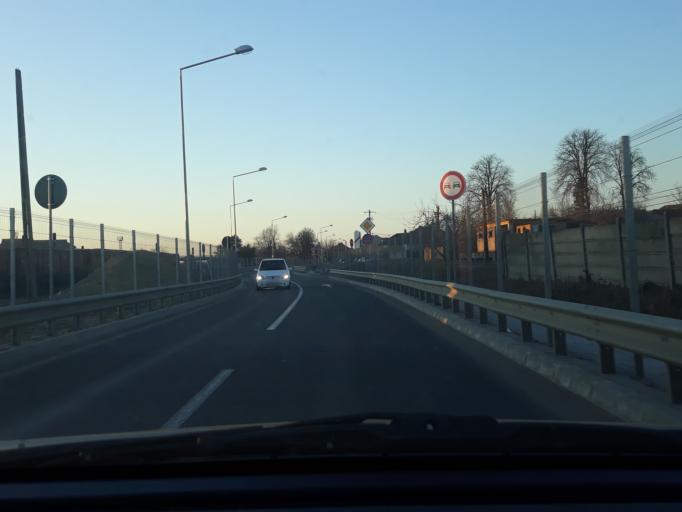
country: RO
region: Bihor
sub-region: Comuna Biharea
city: Oradea
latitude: 47.0758
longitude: 21.9334
